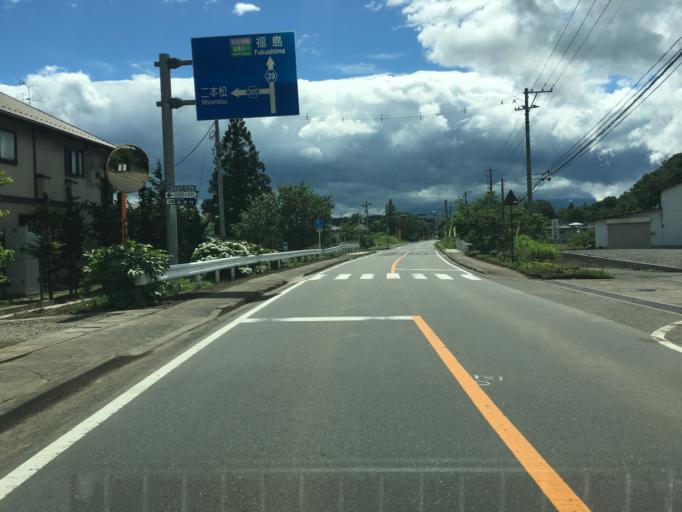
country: JP
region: Fukushima
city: Fukushima-shi
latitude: 37.6581
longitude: 140.5425
